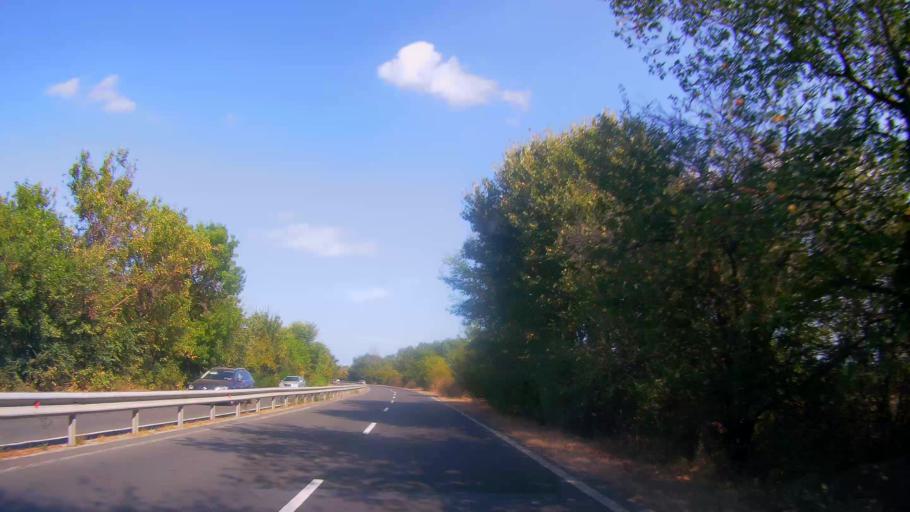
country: BG
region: Burgas
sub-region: Obshtina Sozopol
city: Chernomorets
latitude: 42.4430
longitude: 27.6170
